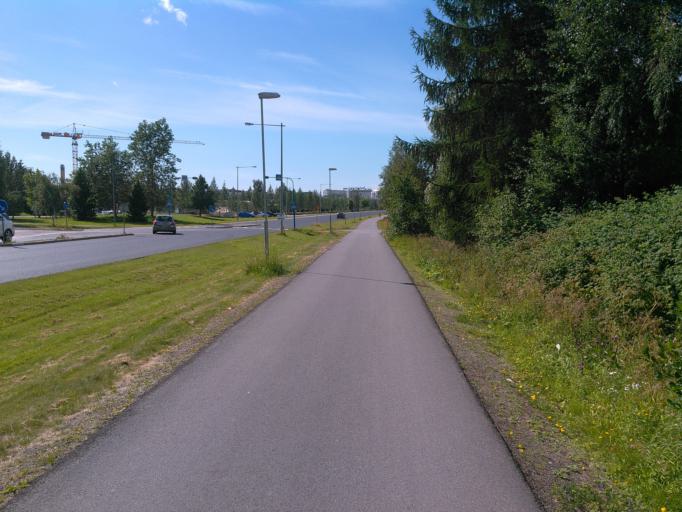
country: SE
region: Vaesterbotten
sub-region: Umea Kommun
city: Umea
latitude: 63.8262
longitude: 20.3094
